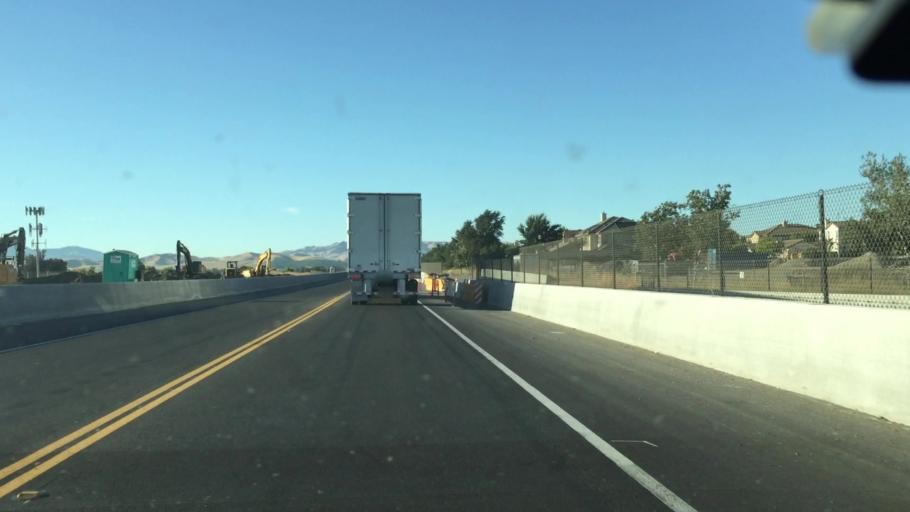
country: US
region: California
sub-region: Alameda County
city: Livermore
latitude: 37.6547
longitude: -121.8055
